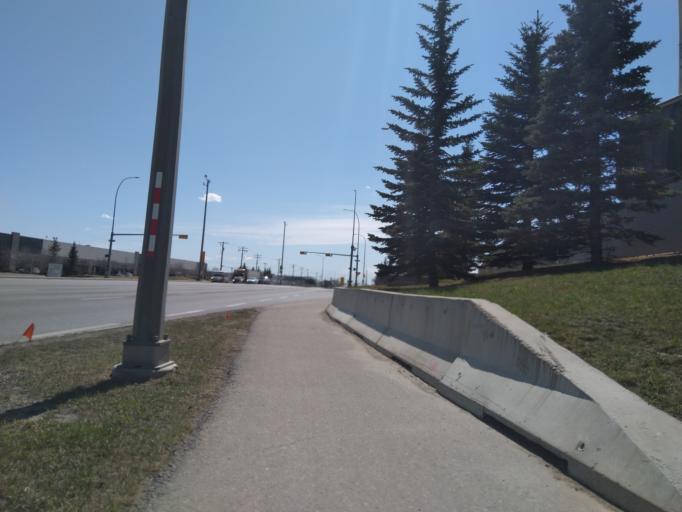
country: CA
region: Alberta
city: Calgary
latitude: 50.9731
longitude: -113.9587
